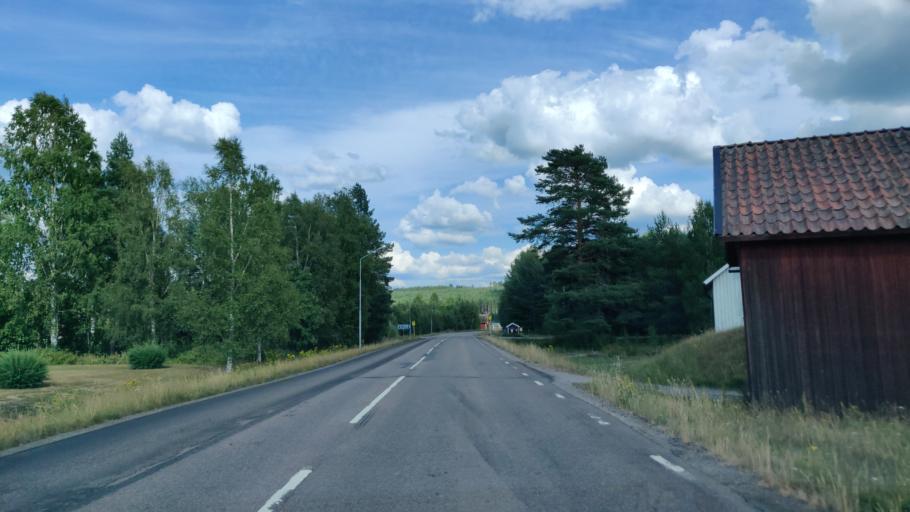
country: SE
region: Vaermland
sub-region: Hagfors Kommun
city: Ekshaerad
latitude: 60.1779
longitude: 13.5104
